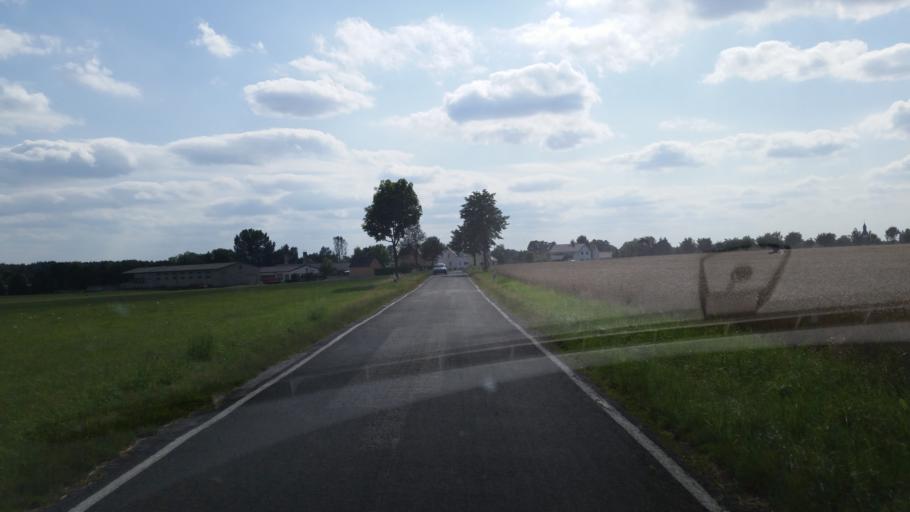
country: DE
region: Saxony
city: Wiednitz
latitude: 51.3500
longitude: 14.0272
